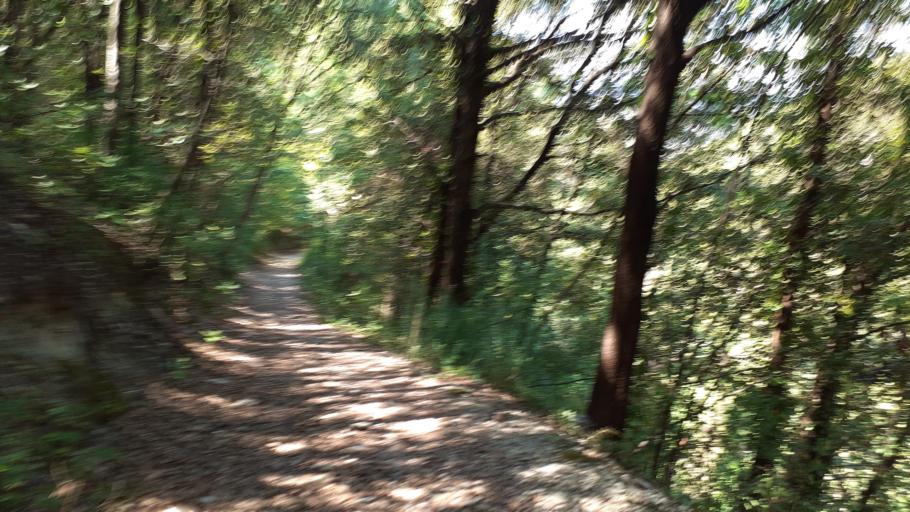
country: IT
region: Abruzzo
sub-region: Provincia di Pescara
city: San Valentino in Abruzzo Citeriore
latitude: 42.2425
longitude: 13.9709
